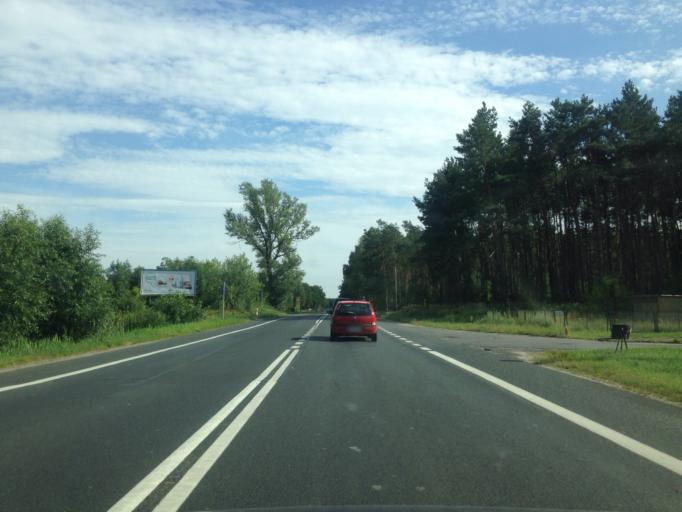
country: PL
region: Kujawsko-Pomorskie
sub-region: Powiat aleksandrowski
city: Aleksandrow Kujawski
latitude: 52.8955
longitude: 18.7288
